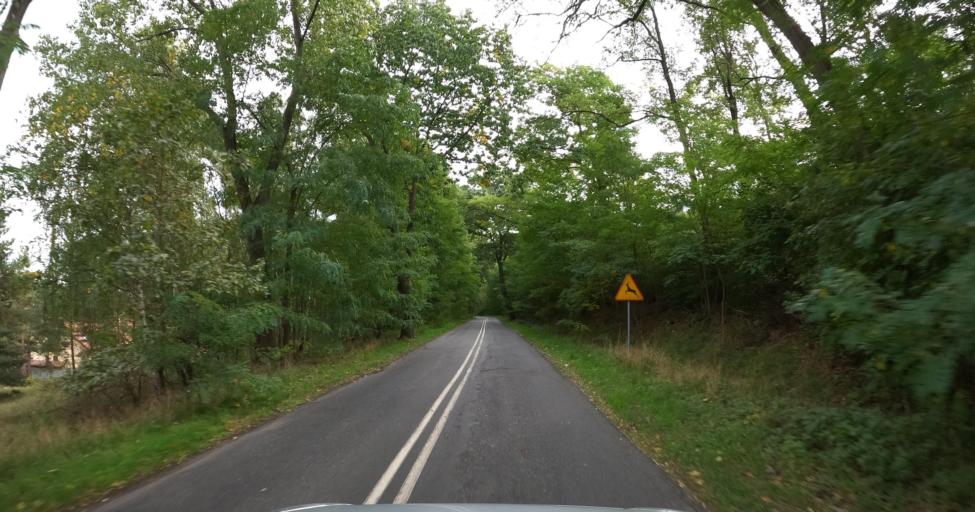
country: PL
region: Lubusz
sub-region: Powiat zielonogorski
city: Zabor
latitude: 51.9484
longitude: 15.6392
